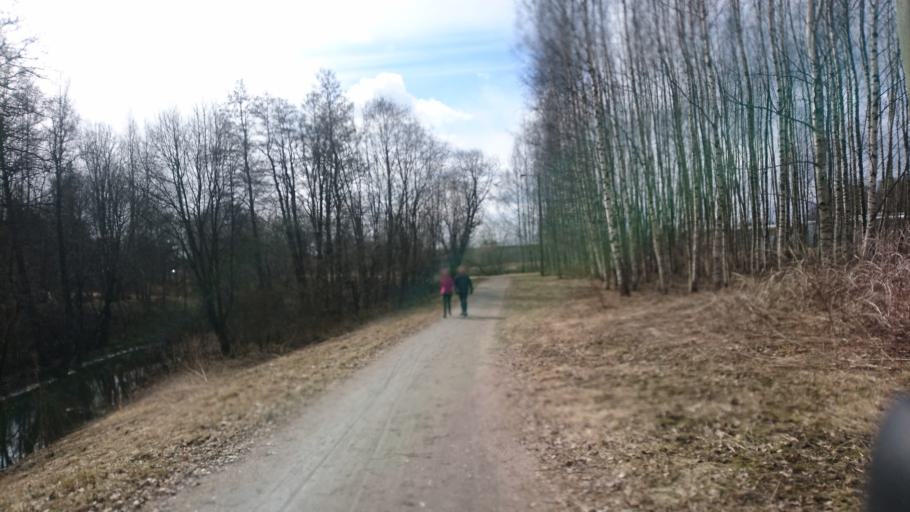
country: FI
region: Uusimaa
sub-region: Helsinki
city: Espoo
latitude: 60.2217
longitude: 24.6617
